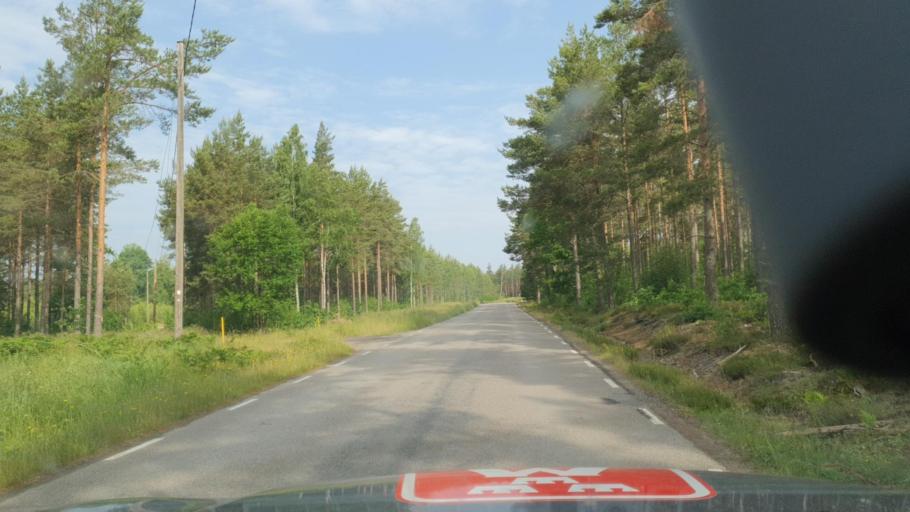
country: SE
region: Kalmar
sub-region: Kalmar Kommun
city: Ljungbyholm
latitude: 56.6062
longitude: 16.0738
